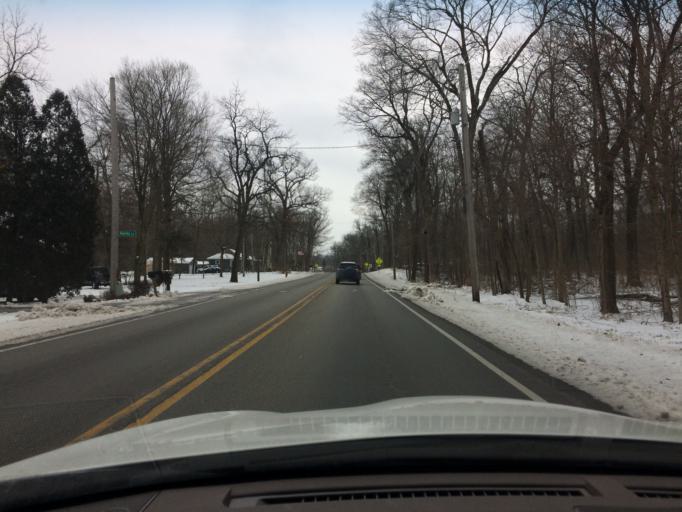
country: US
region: Illinois
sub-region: Kane County
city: Sugar Grove
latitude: 41.7855
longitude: -88.4359
